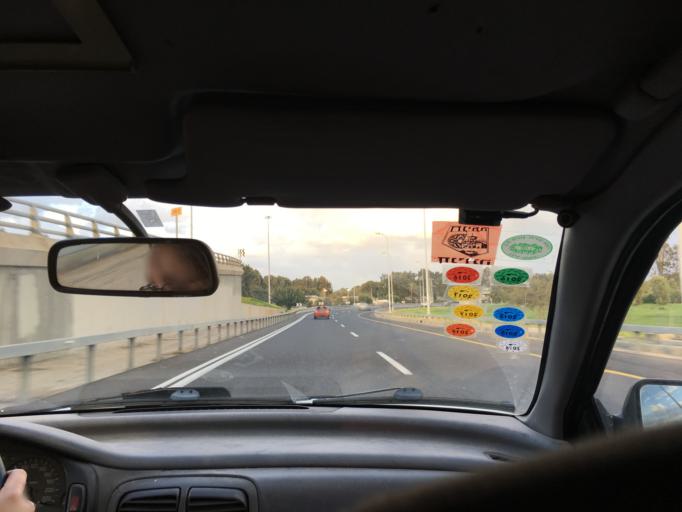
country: IL
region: Tel Aviv
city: Ramat HaSharon
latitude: 32.1369
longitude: 34.8123
